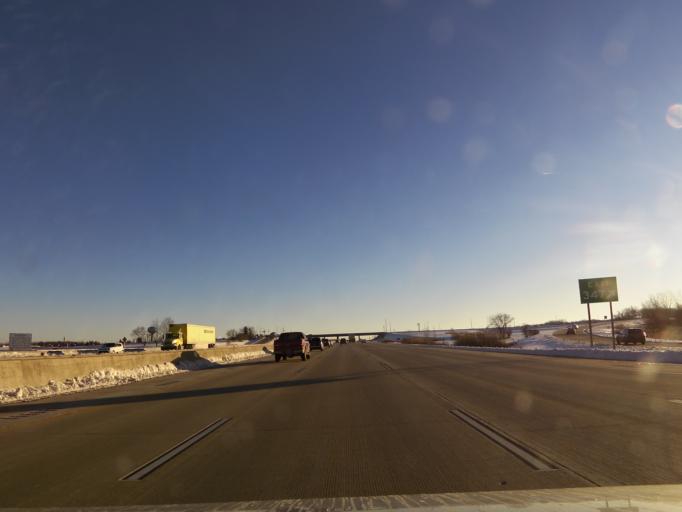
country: US
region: Wisconsin
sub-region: Kenosha County
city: Pleasant Prairie
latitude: 42.5286
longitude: -87.9521
